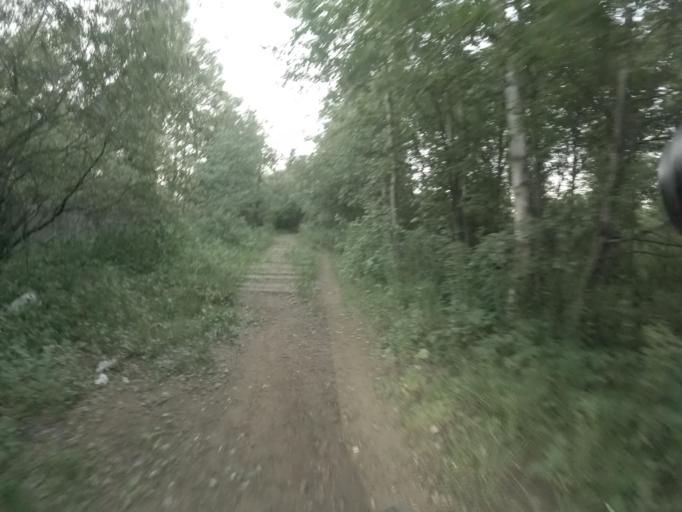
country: RU
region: St.-Petersburg
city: Krasnogvargeisky
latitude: 59.9902
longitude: 30.5325
